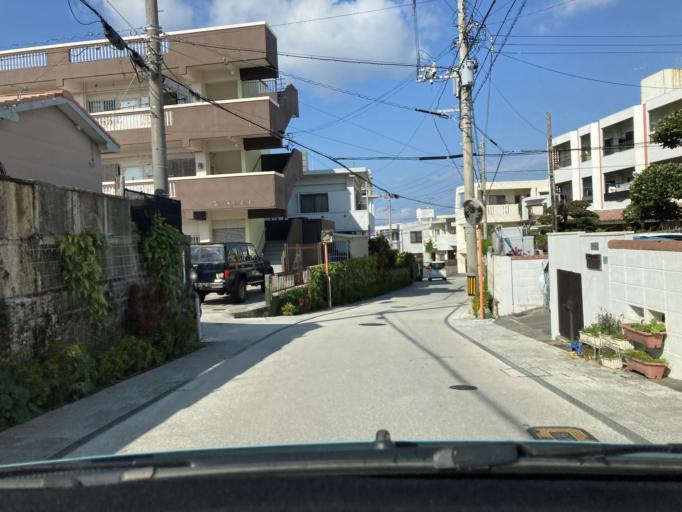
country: JP
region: Okinawa
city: Ginowan
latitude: 26.2488
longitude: 127.7275
